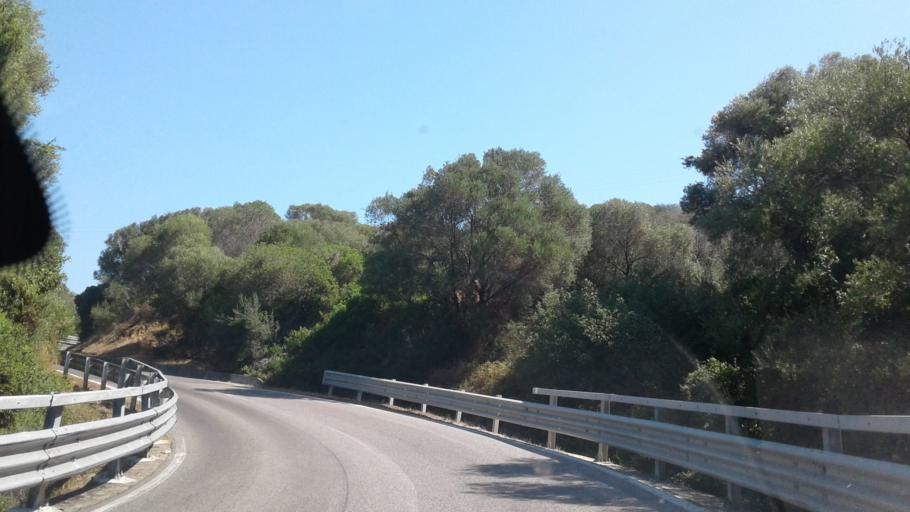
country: IT
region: Sardinia
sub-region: Provincia di Olbia-Tempio
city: Palau
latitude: 41.1676
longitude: 9.3174
